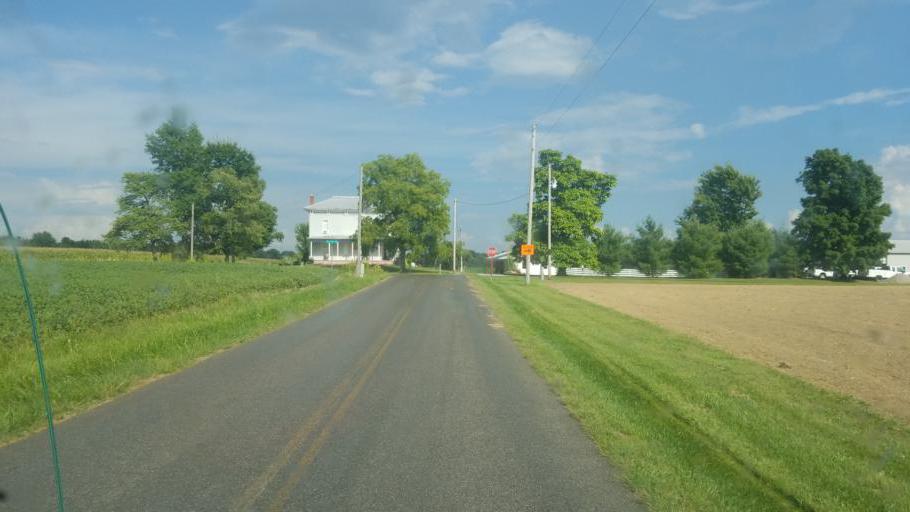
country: US
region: Ohio
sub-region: Huron County
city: Plymouth
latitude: 41.0067
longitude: -82.6075
